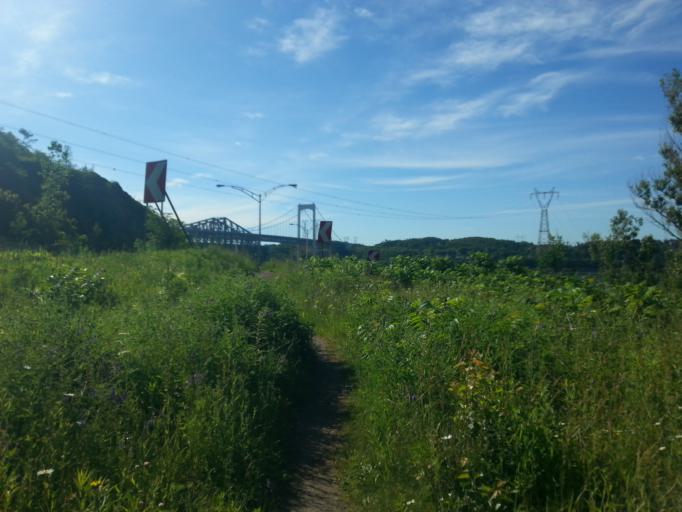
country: CA
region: Quebec
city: L'Ancienne-Lorette
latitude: 46.7496
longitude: -71.2991
